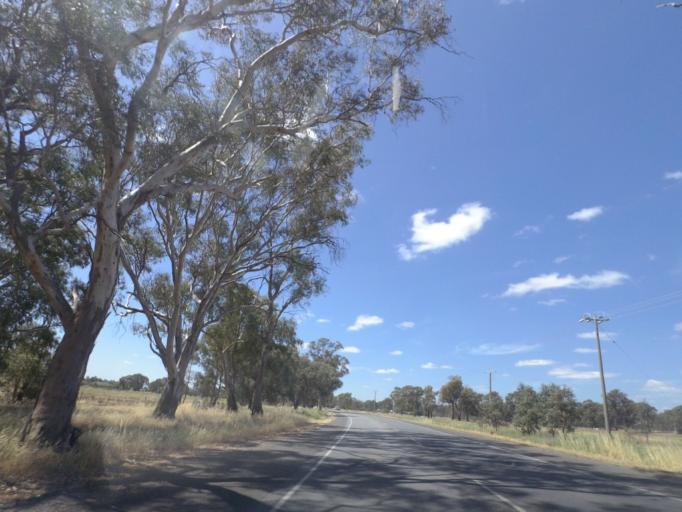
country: AU
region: Victoria
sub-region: Wangaratta
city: Wangaratta
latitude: -36.3998
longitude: 146.2777
